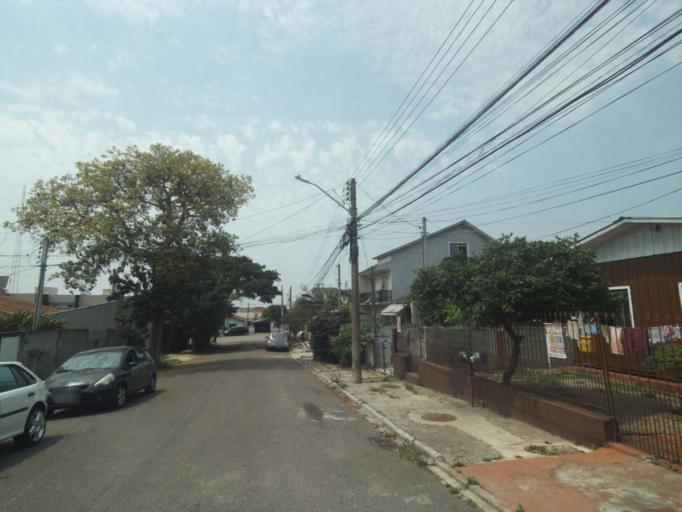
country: BR
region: Parana
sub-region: Sao Jose Dos Pinhais
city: Sao Jose dos Pinhais
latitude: -25.5373
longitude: -49.2432
